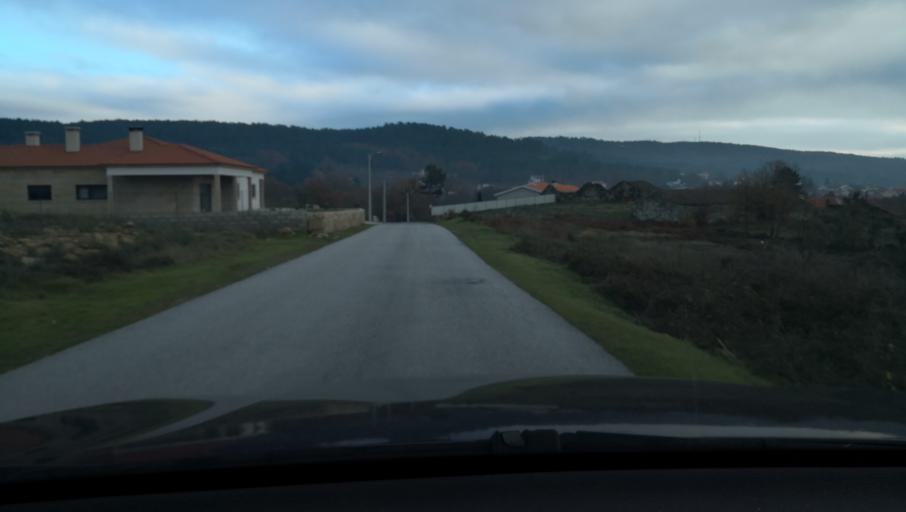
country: PT
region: Vila Real
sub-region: Vila Real
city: Vila Real
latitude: 41.3443
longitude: -7.6635
